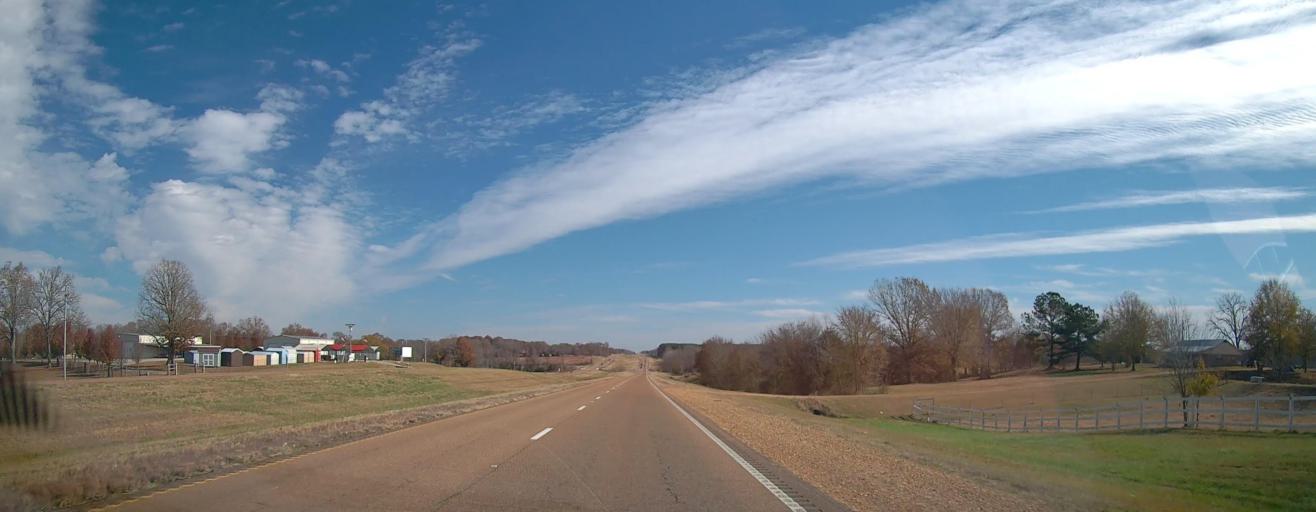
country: US
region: Mississippi
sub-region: Marshall County
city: Holly Springs
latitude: 34.9462
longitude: -89.3832
